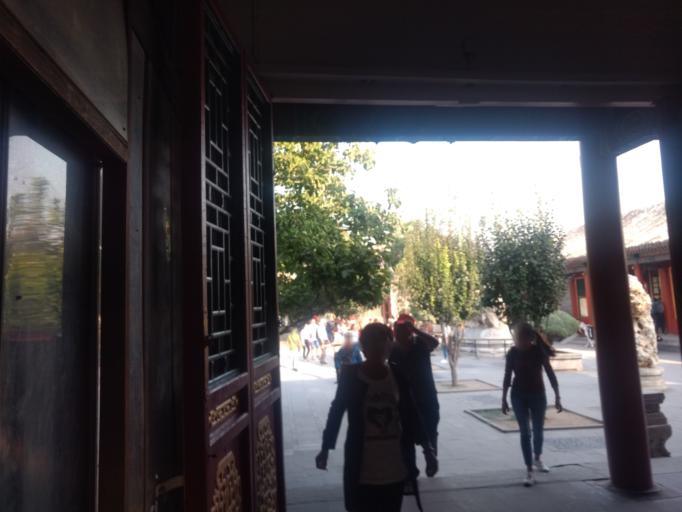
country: CN
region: Beijing
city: Haidian
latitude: 39.9973
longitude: 116.2720
